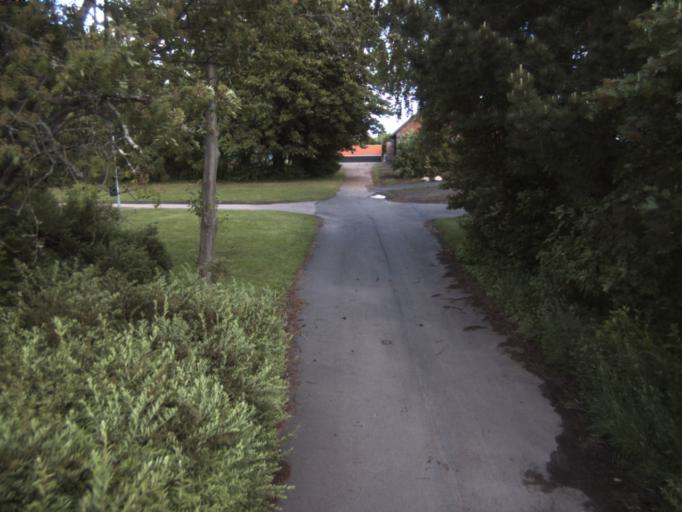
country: SE
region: Skane
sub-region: Helsingborg
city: Helsingborg
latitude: 56.0278
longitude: 12.7515
